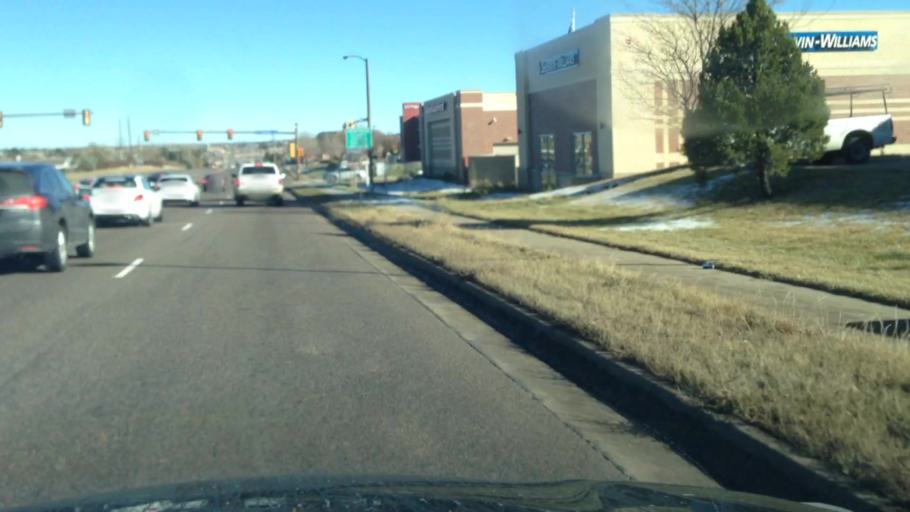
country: US
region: Colorado
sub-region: Arapahoe County
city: Dove Valley
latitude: 39.5949
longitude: -104.8325
